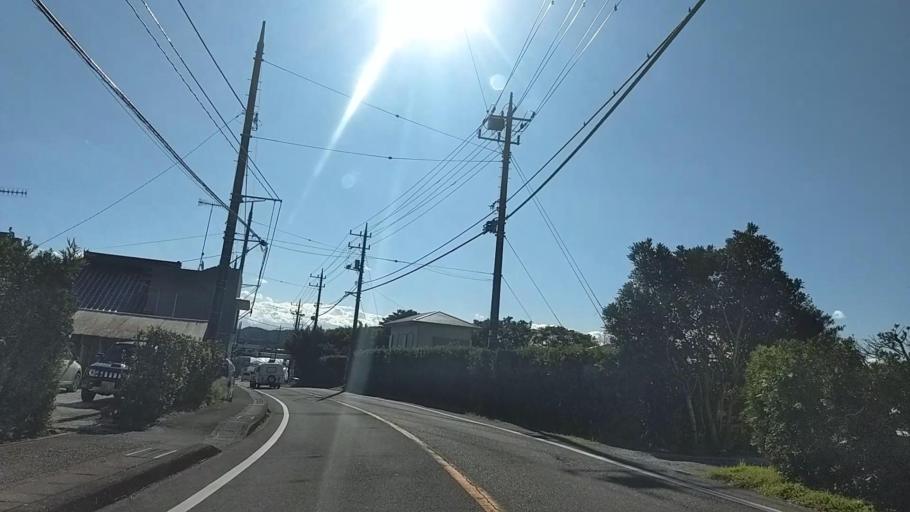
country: JP
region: Chiba
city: Tateyama
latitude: 34.9440
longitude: 139.8367
